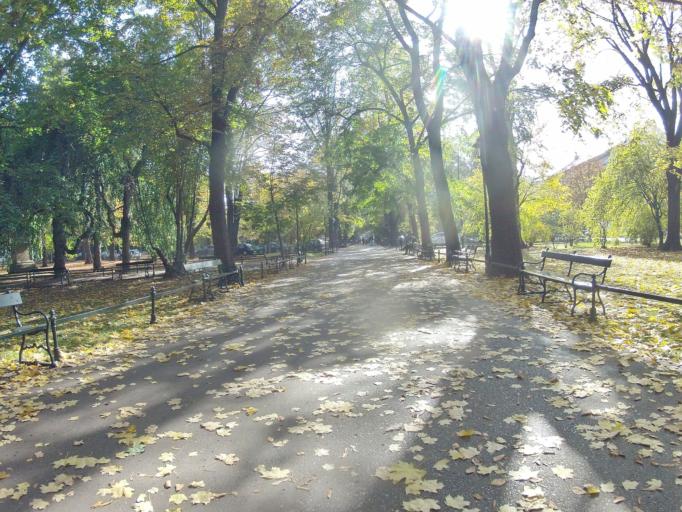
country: PL
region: Lesser Poland Voivodeship
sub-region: Krakow
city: Krakow
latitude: 50.0583
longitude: 19.9339
